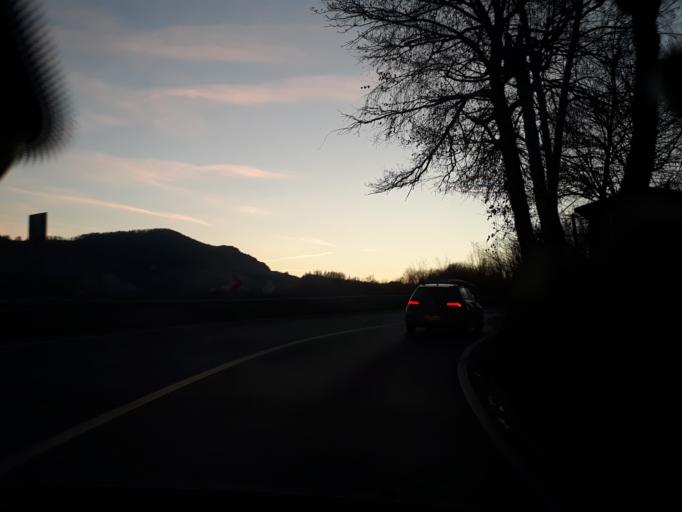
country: BA
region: Federation of Bosnia and Herzegovina
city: Hadzici
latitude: 43.8789
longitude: 18.1974
